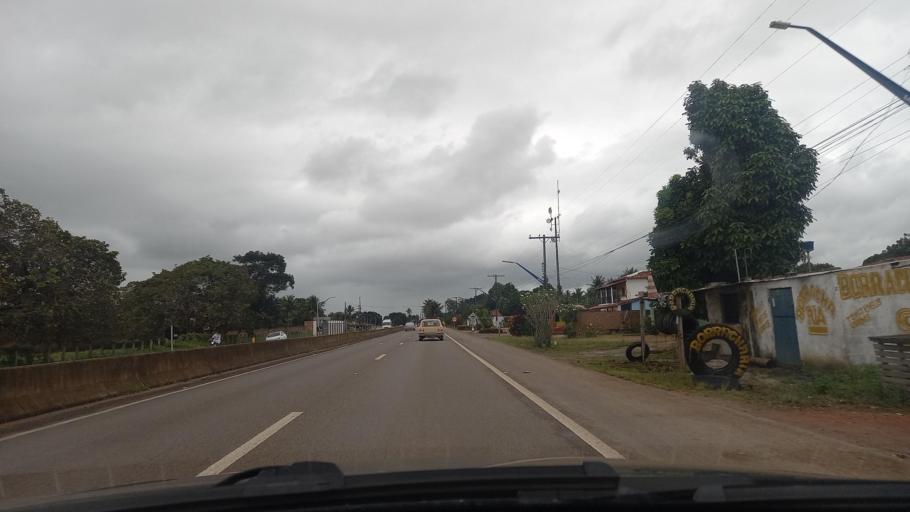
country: BR
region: Alagoas
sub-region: Limoeiro De Anadia
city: Cajueiro
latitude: -9.7518
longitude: -36.4517
